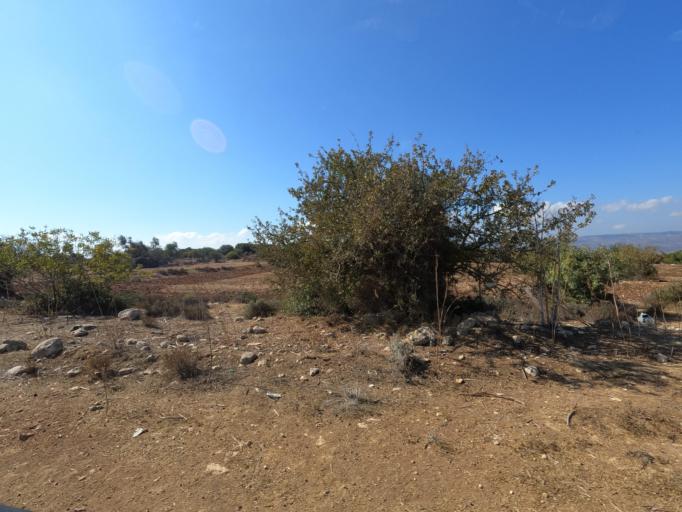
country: CY
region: Pafos
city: Polis
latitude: 34.9835
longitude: 32.5051
